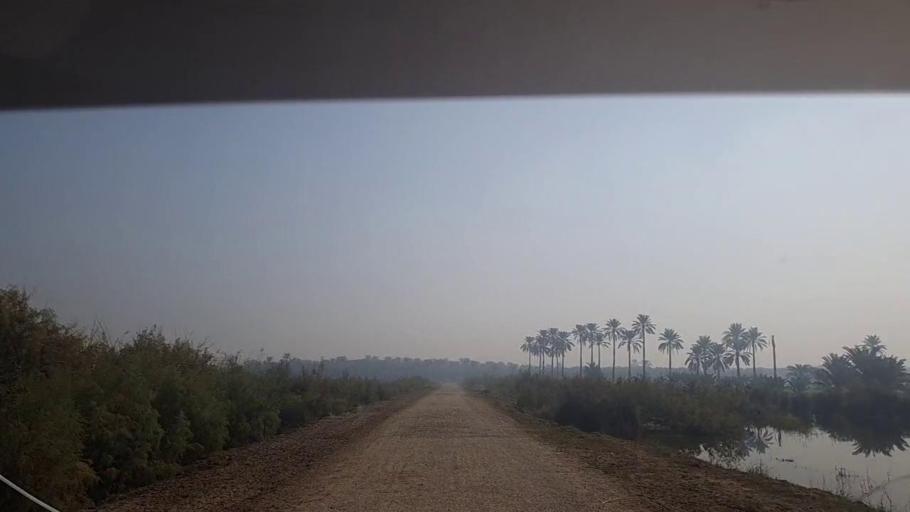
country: PK
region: Sindh
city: Khairpur
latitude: 27.4800
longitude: 68.7164
